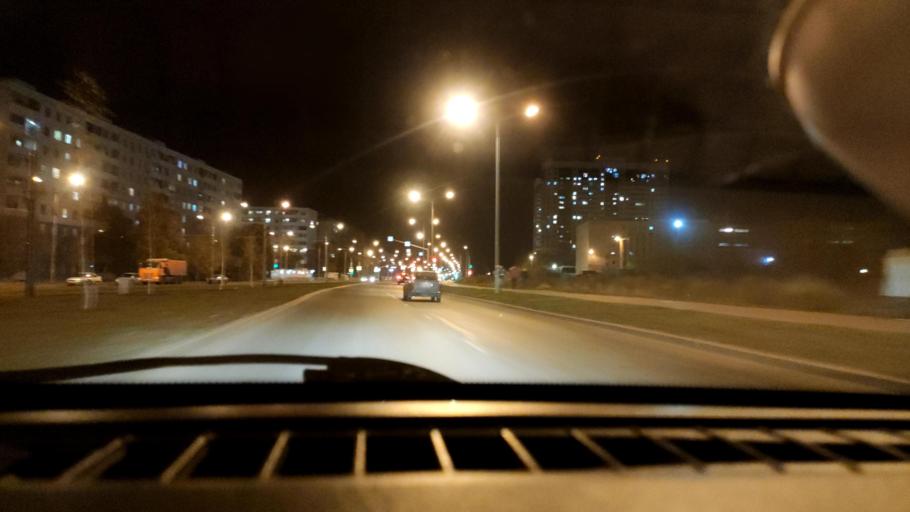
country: RU
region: Samara
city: Samara
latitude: 53.2630
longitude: 50.2366
